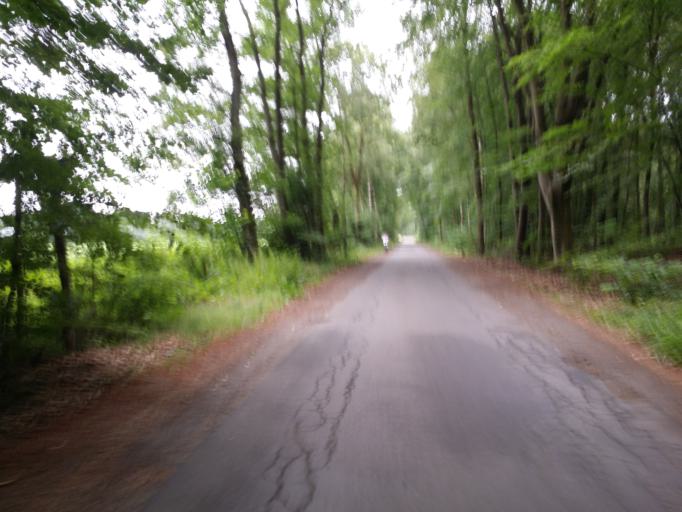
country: DE
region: Lower Saxony
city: Reppenstedt
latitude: 53.2324
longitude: 10.3355
